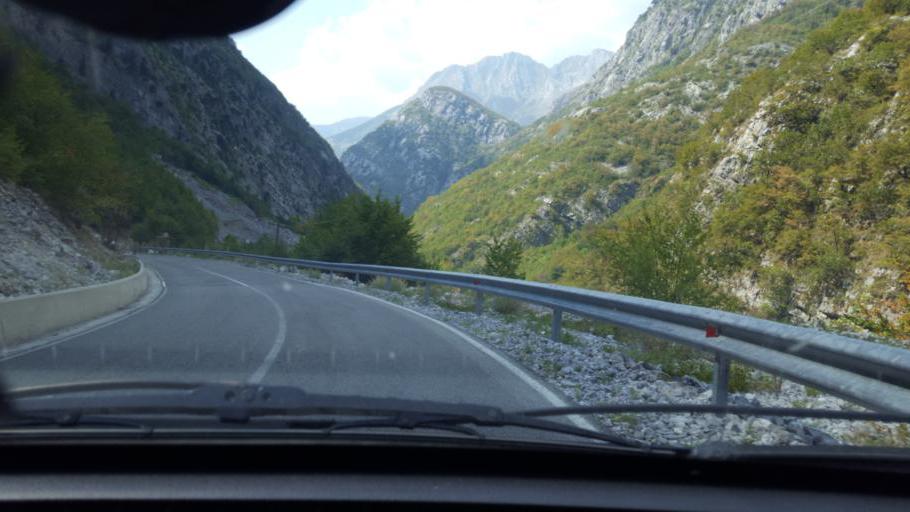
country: ME
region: Andrijevica
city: Andrijevica
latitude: 42.5334
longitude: 19.6607
